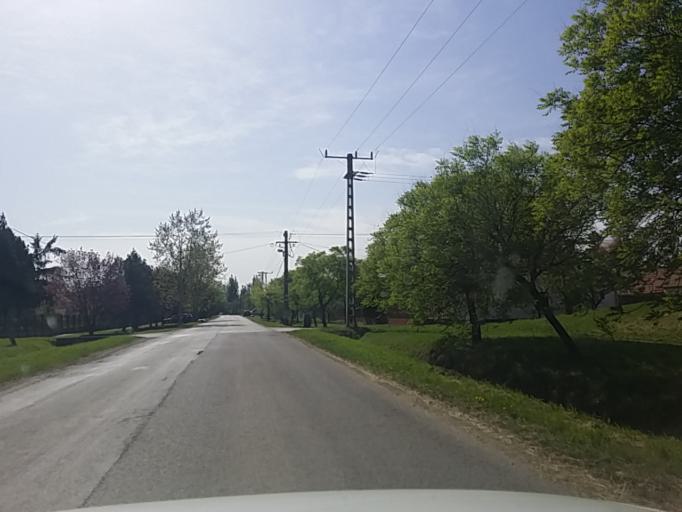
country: HU
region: Bekes
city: Doboz
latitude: 46.7028
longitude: 21.1827
